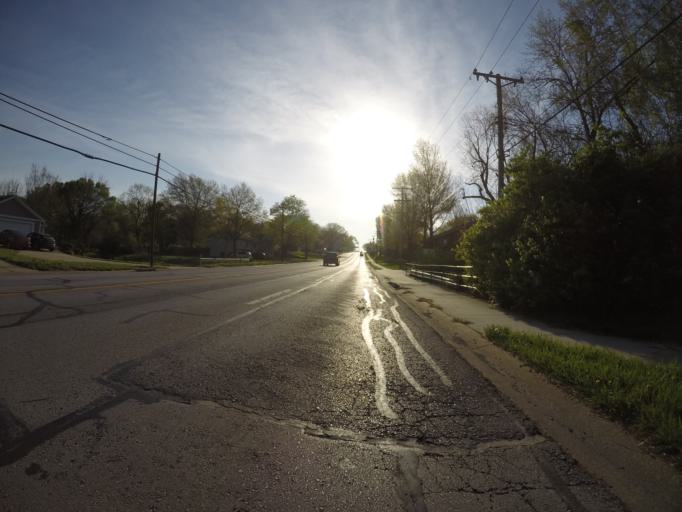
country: US
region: Missouri
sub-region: Jackson County
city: Lees Summit
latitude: 38.9114
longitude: -94.4036
